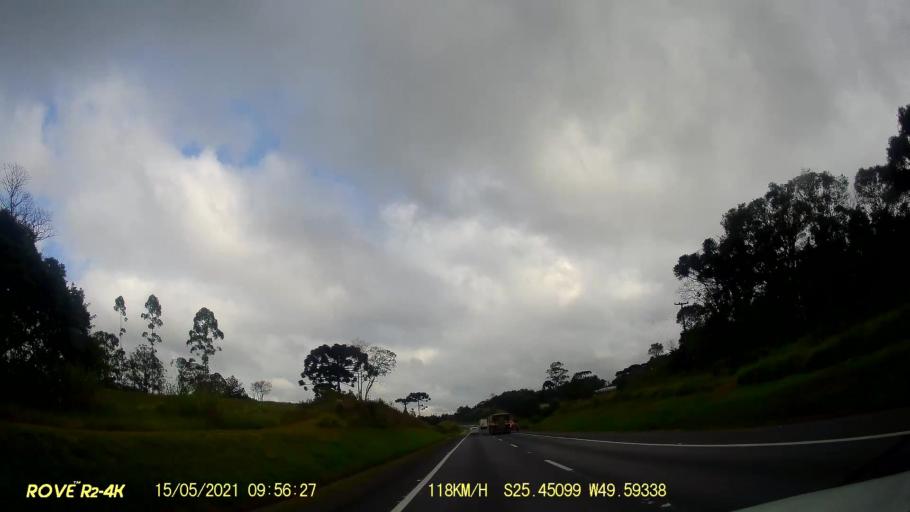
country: BR
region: Parana
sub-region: Campo Largo
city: Campo Largo
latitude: -25.4511
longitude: -49.5940
